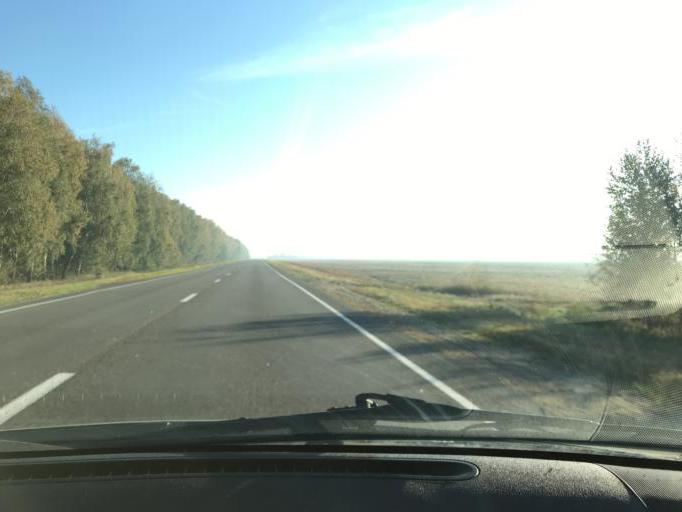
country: BY
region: Brest
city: Asnyezhytsy
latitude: 52.2658
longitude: 26.3384
